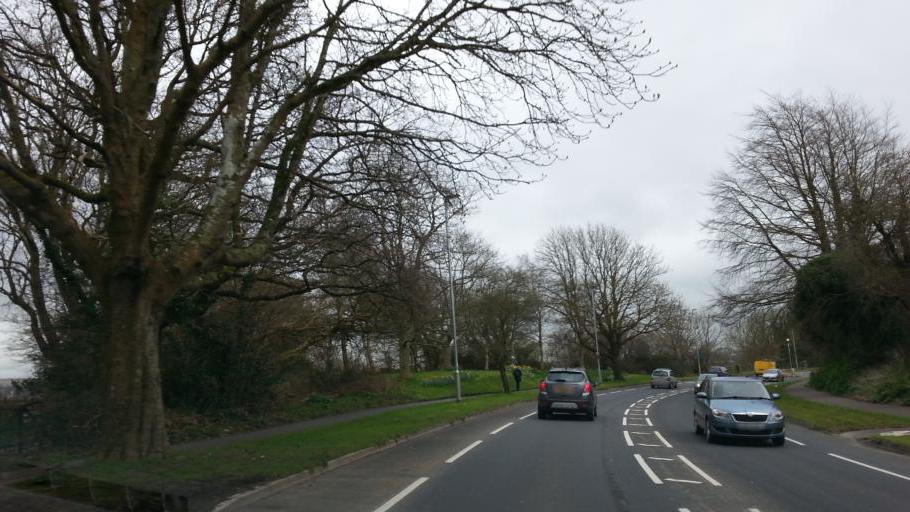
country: GB
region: England
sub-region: Devon
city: Barnstaple
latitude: 51.0900
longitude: -4.0528
